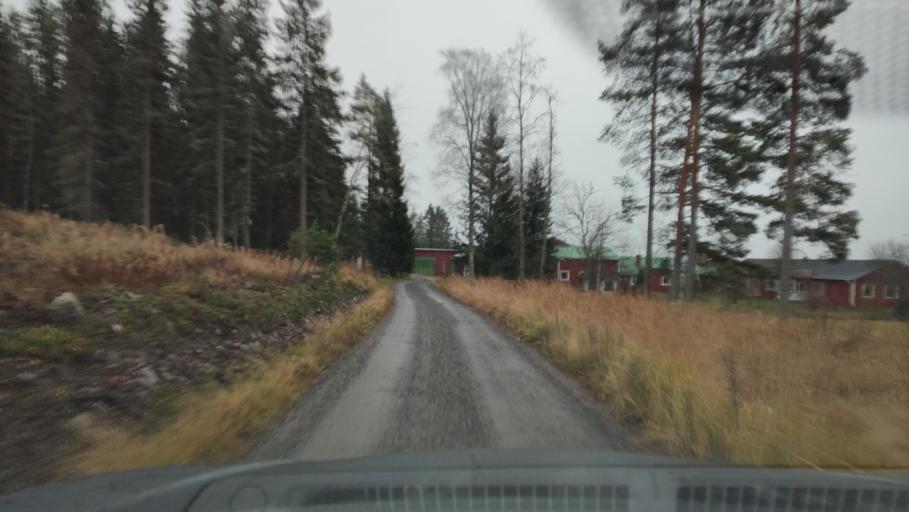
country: FI
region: Southern Ostrobothnia
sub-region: Suupohja
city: Karijoki
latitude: 62.2236
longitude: 21.5690
